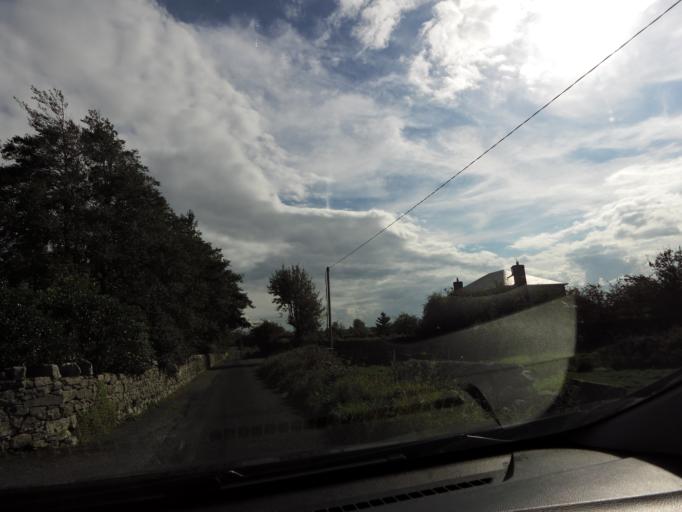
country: IE
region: Connaught
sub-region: County Galway
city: Athenry
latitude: 53.3106
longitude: -8.7431
